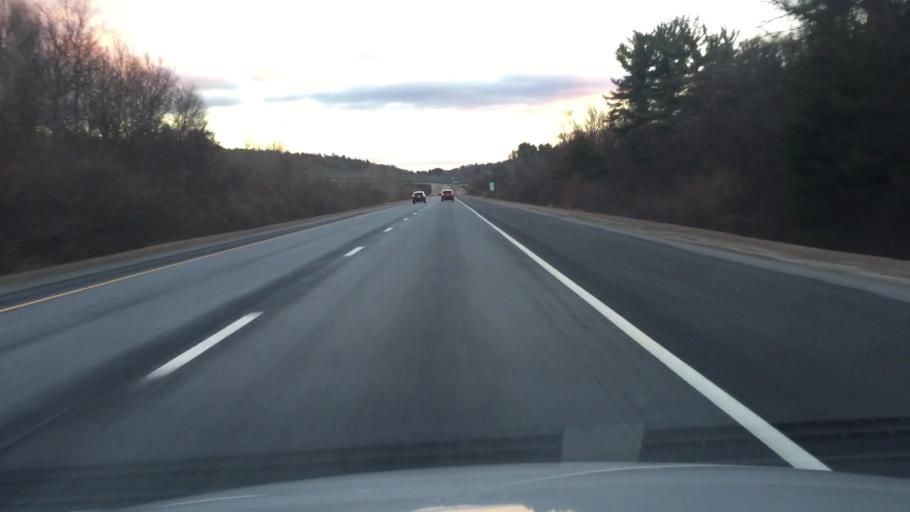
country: US
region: Massachusetts
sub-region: Worcester County
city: West Boylston
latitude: 42.3638
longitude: -71.8155
